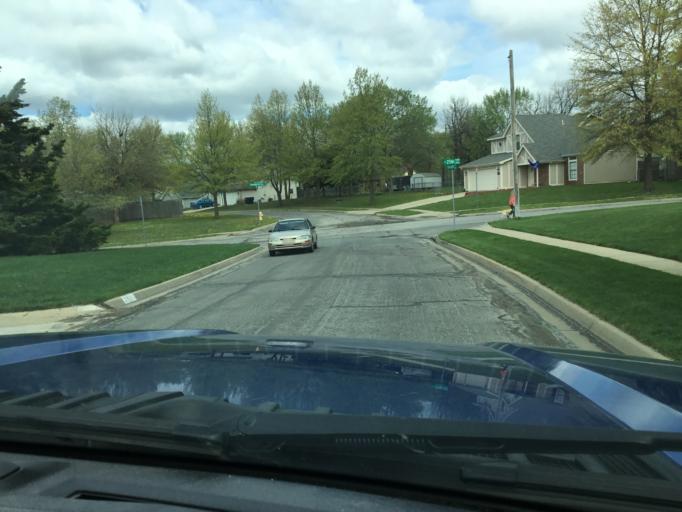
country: US
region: Kansas
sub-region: Douglas County
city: Lawrence
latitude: 38.9383
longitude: -95.2103
